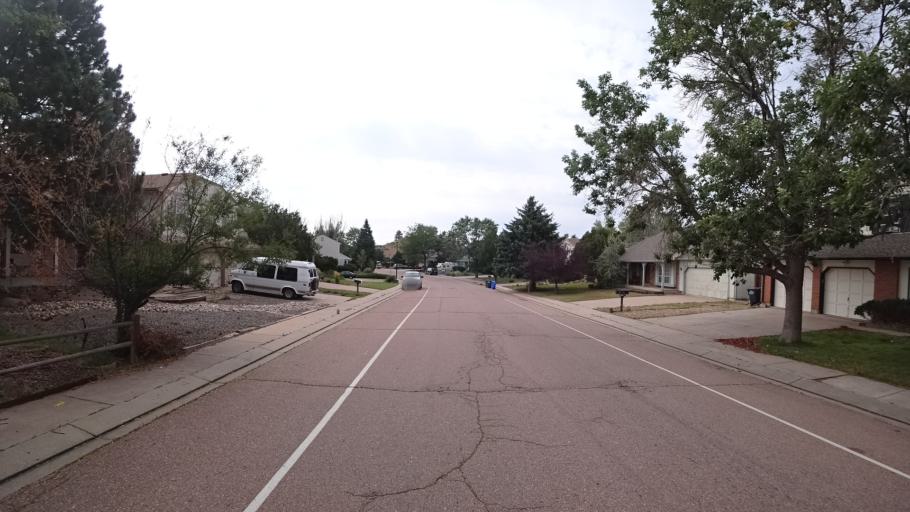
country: US
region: Colorado
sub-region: El Paso County
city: Air Force Academy
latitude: 38.9205
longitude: -104.8287
